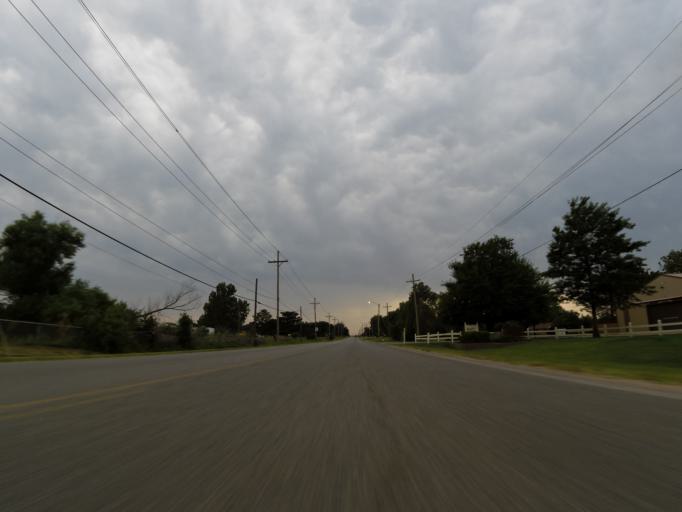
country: US
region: Kansas
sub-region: Reno County
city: South Hutchinson
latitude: 38.0280
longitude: -97.9619
